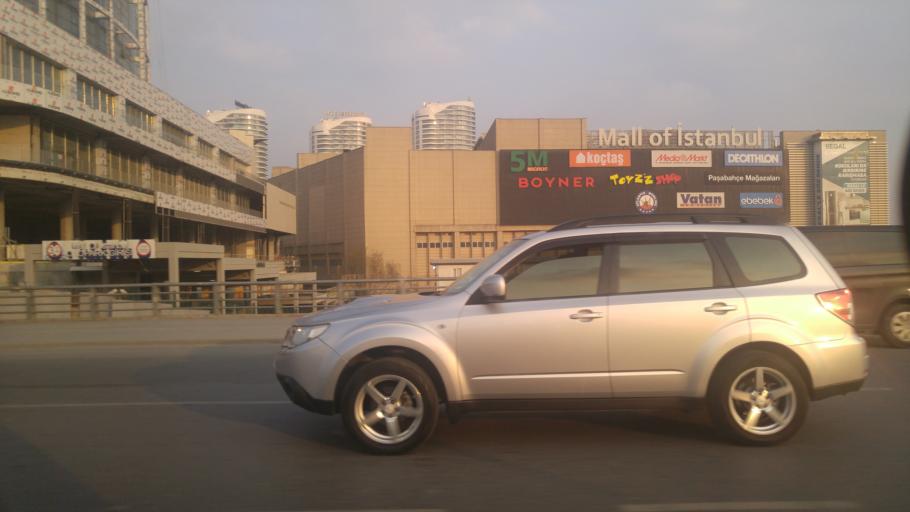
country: TR
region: Istanbul
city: Mahmutbey
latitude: 41.0634
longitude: 28.8035
